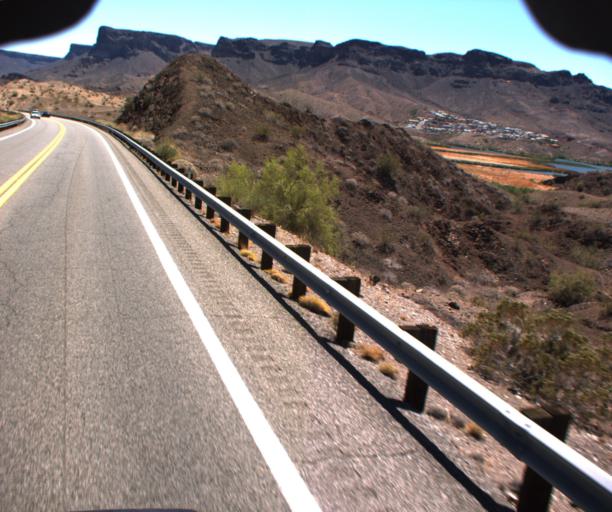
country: US
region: Arizona
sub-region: La Paz County
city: Cienega Springs
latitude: 34.3069
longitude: -114.0990
